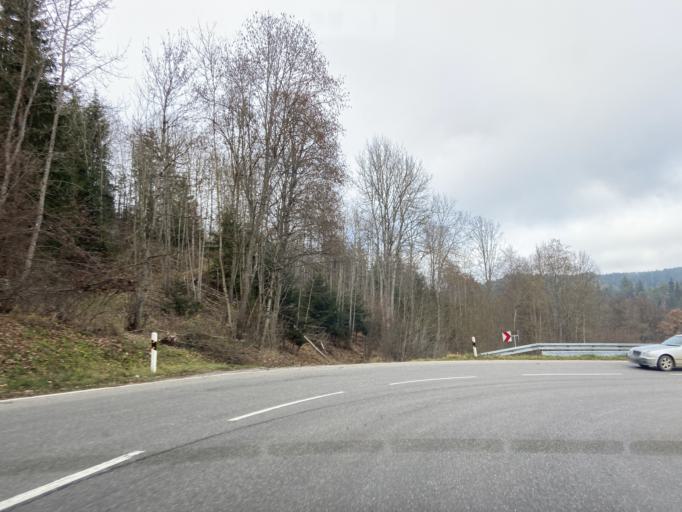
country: DE
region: Baden-Wuerttemberg
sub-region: Tuebingen Region
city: Gammertingen
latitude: 48.2523
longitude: 9.2093
